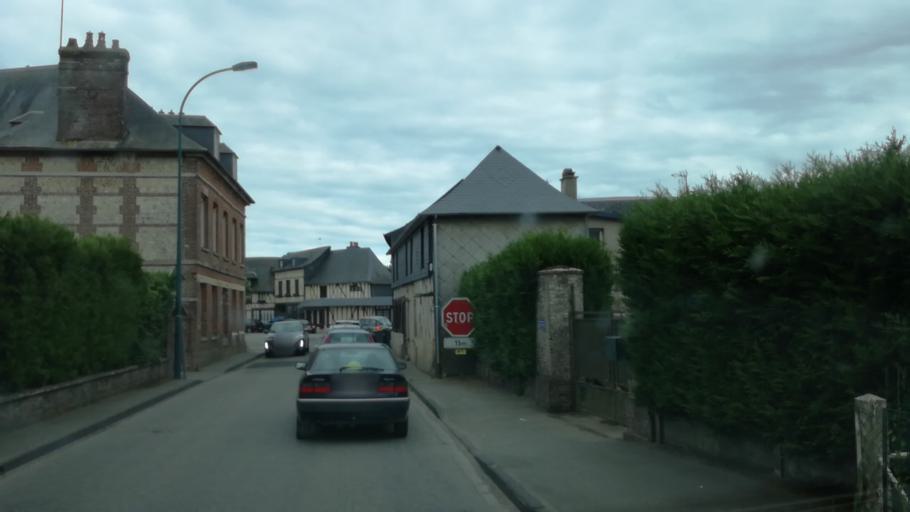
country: FR
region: Haute-Normandie
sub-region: Departement de l'Eure
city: Bourgtheroulde-Infreville
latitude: 49.2267
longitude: 0.8411
